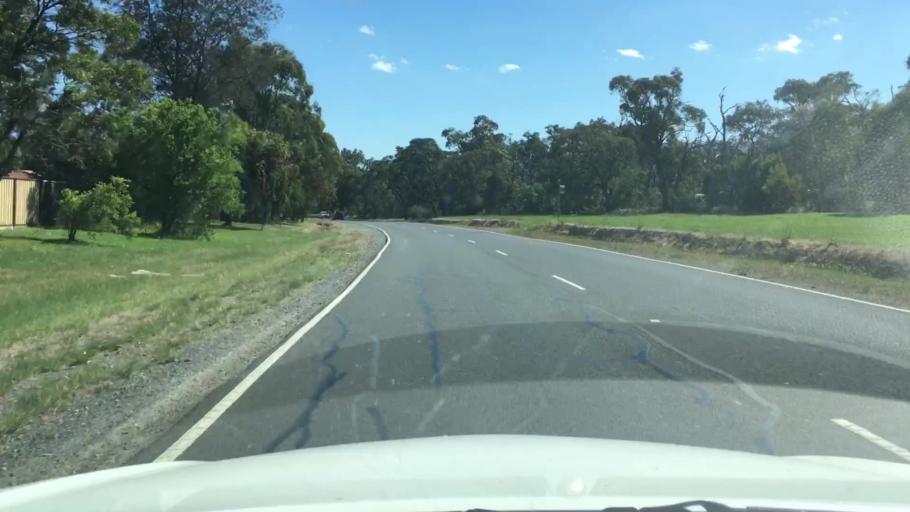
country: AU
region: Victoria
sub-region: Yarra Ranges
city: Lysterfield
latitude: -37.9243
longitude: 145.2693
